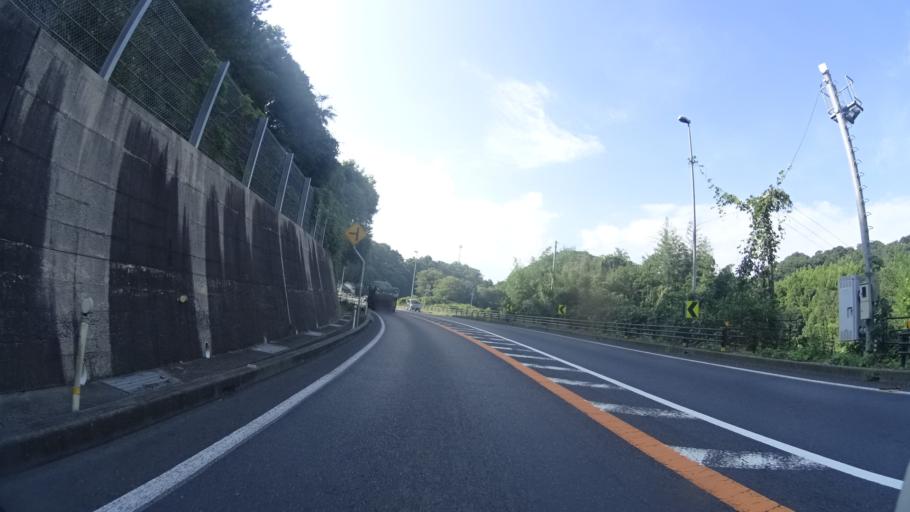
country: JP
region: Shimane
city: Odacho-oda
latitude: 35.2593
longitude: 132.5767
